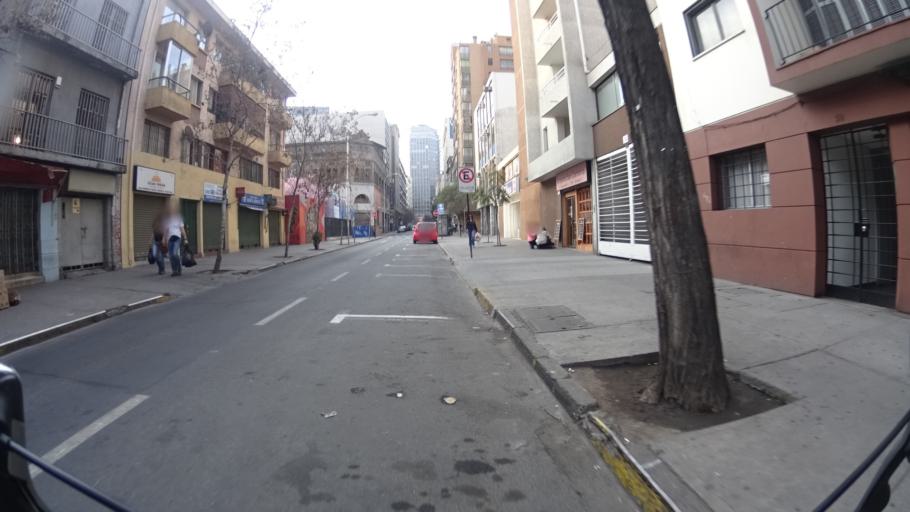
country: CL
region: Santiago Metropolitan
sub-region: Provincia de Santiago
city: Santiago
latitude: -33.4464
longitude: -70.6490
